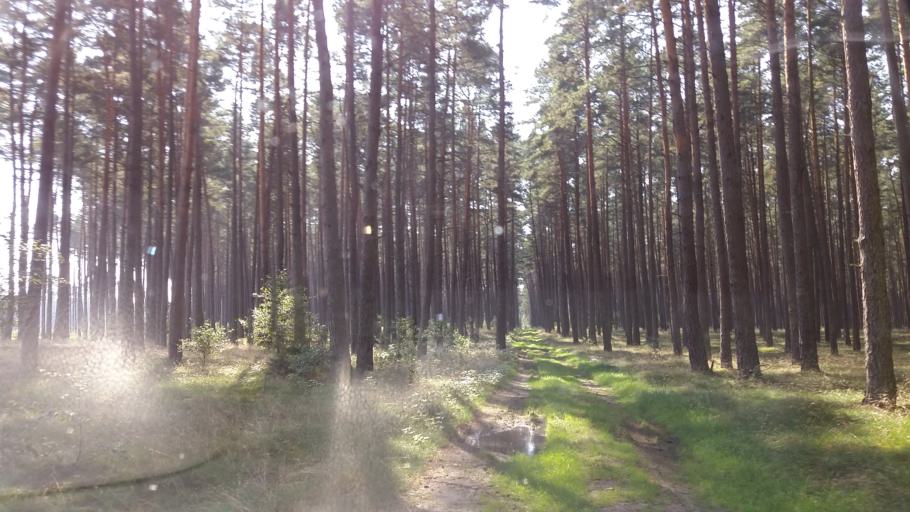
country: PL
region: West Pomeranian Voivodeship
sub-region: Powiat walecki
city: Tuczno
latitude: 53.2209
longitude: 16.0207
